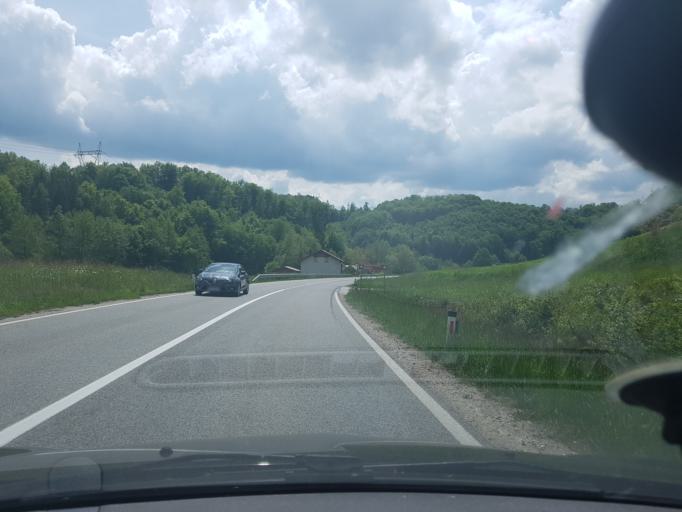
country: SI
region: Rogaska Slatina
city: Rogaska Slatina
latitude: 46.2434
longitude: 15.6057
